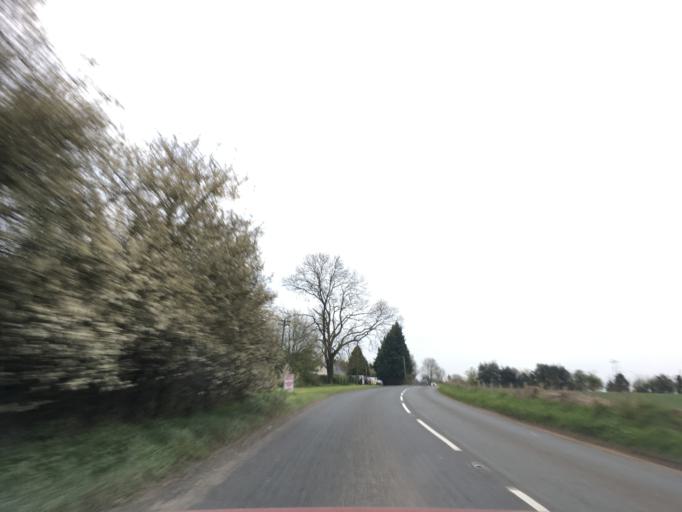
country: GB
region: England
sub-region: Gloucestershire
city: Nailsworth
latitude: 51.6382
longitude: -2.2495
